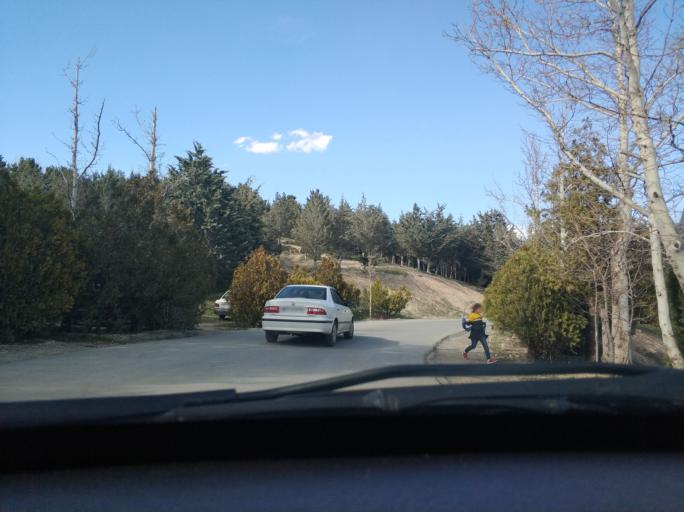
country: IR
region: Tehran
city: Tajrish
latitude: 35.8047
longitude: 51.5689
